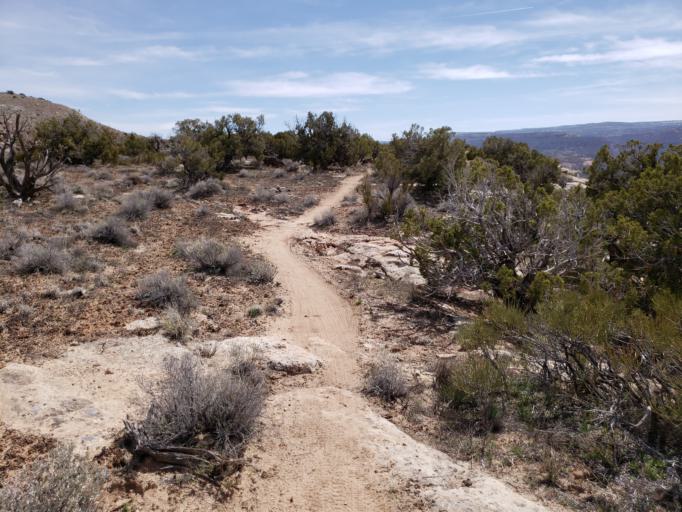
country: US
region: Colorado
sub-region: Mesa County
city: Loma
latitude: 39.1848
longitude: -108.8693
